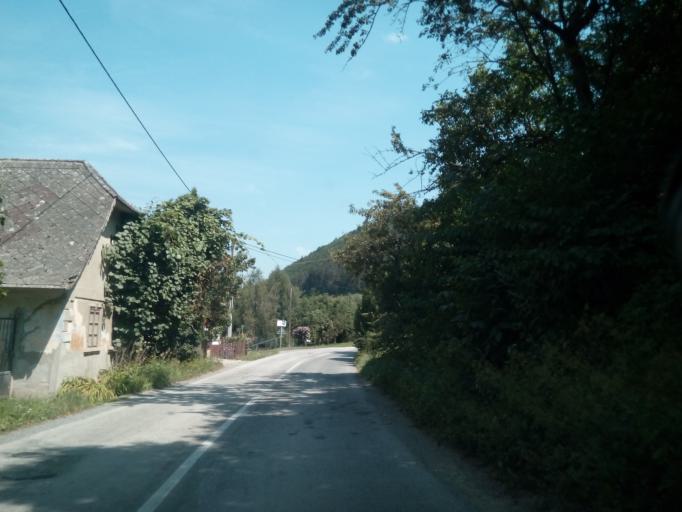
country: SK
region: Kosicky
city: Kosice
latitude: 48.8321
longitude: 21.2192
